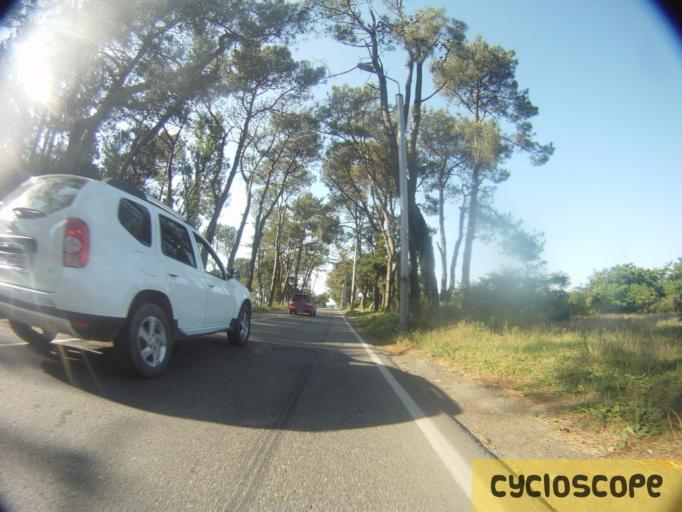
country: GE
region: Ajaria
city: Kobuleti
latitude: 41.8877
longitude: 41.7741
